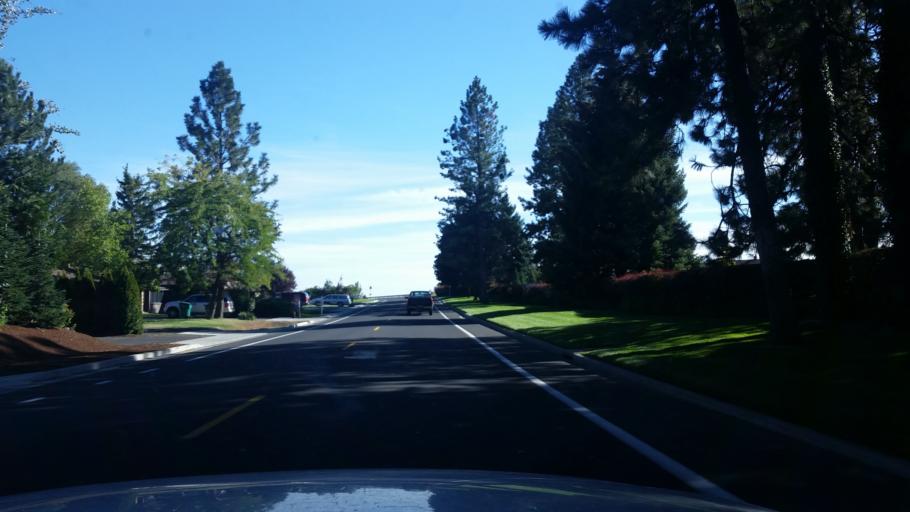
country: US
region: Washington
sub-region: Spokane County
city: Spokane
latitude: 47.6050
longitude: -117.3953
